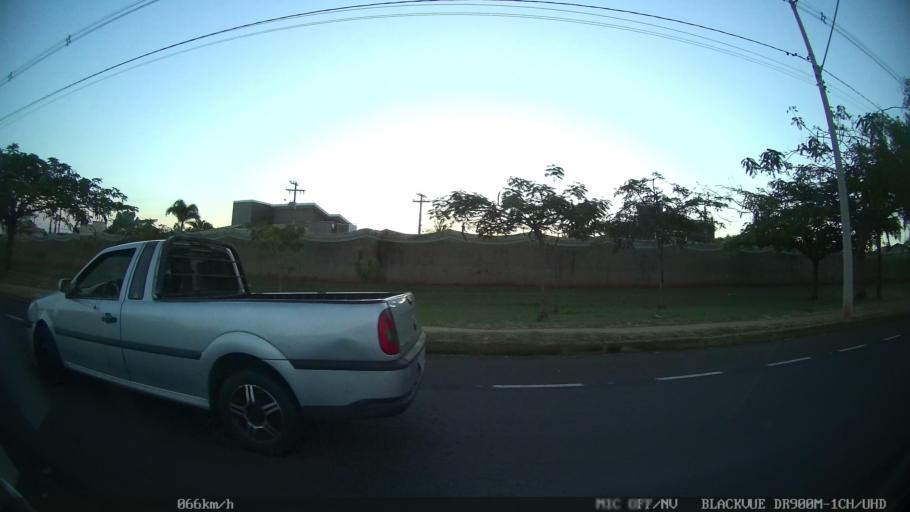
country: BR
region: Sao Paulo
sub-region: Sao Jose Do Rio Preto
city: Sao Jose do Rio Preto
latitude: -20.8198
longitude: -49.3399
